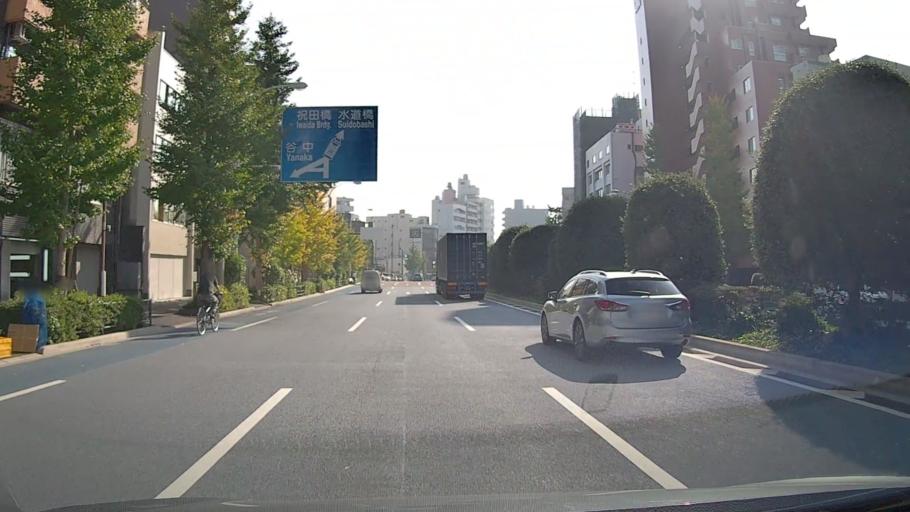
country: JP
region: Tokyo
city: Tokyo
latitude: 35.7207
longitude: 139.7501
